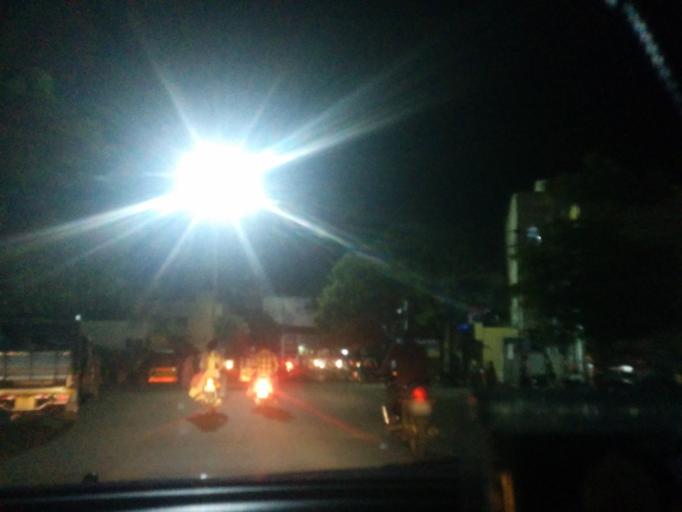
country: IN
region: Andhra Pradesh
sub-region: East Godavari
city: Rajahmundry
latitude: 17.0112
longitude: 81.7723
